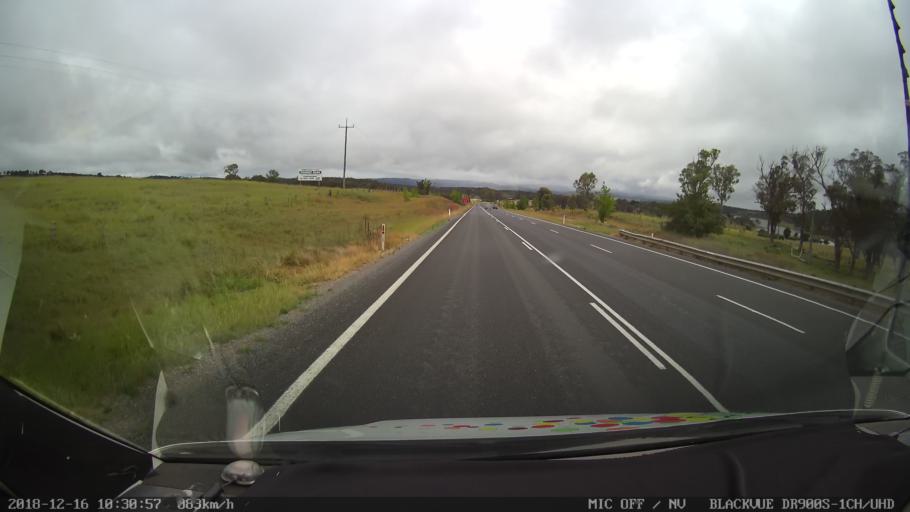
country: AU
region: New South Wales
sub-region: Tenterfield Municipality
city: Carrolls Creek
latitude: -29.0865
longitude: 152.0037
